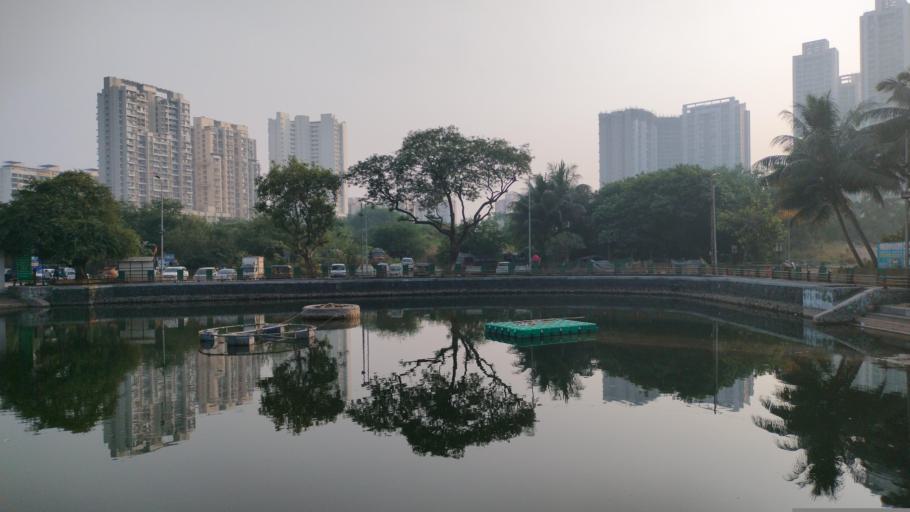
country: IN
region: Maharashtra
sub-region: Thane
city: Airoli
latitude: 19.1220
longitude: 72.9961
